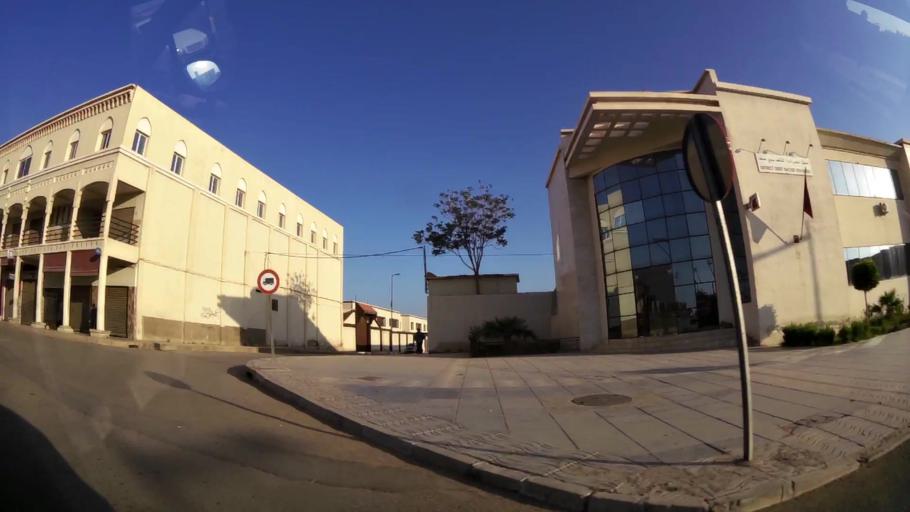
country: MA
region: Oriental
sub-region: Oujda-Angad
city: Oujda
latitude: 34.6744
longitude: -1.9314
